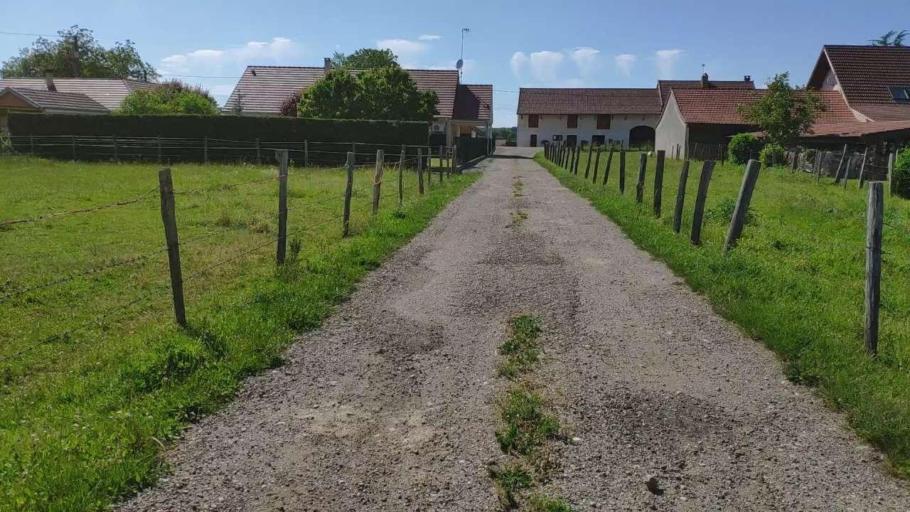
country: FR
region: Franche-Comte
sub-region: Departement du Jura
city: Bletterans
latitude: 46.7598
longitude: 5.4709
